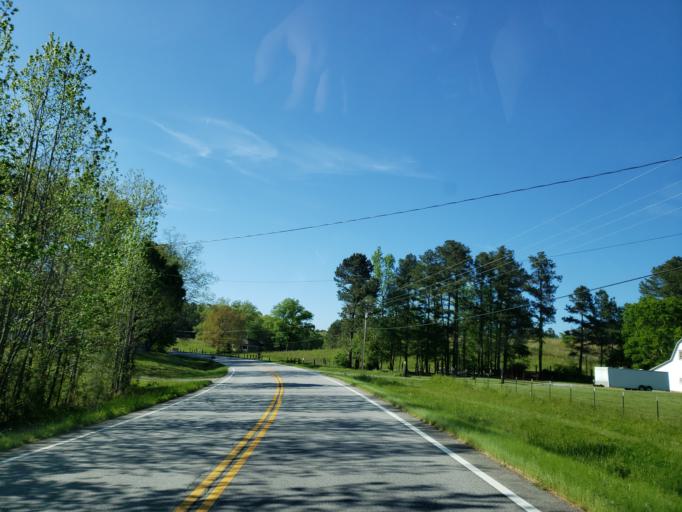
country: US
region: Georgia
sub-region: Haralson County
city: Tallapoosa
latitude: 33.8739
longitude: -85.3014
